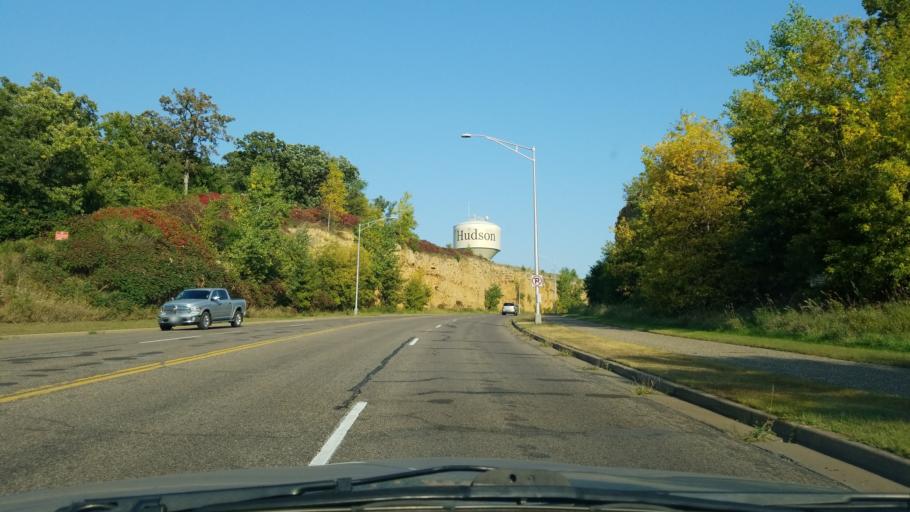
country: US
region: Wisconsin
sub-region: Saint Croix County
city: Hudson
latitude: 44.9546
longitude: -92.7184
